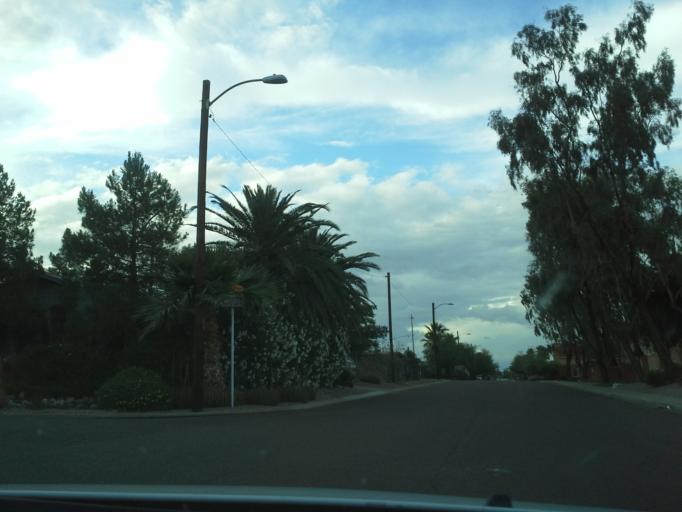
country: US
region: Arizona
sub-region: Maricopa County
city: Phoenix
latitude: 33.5461
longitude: -112.0542
